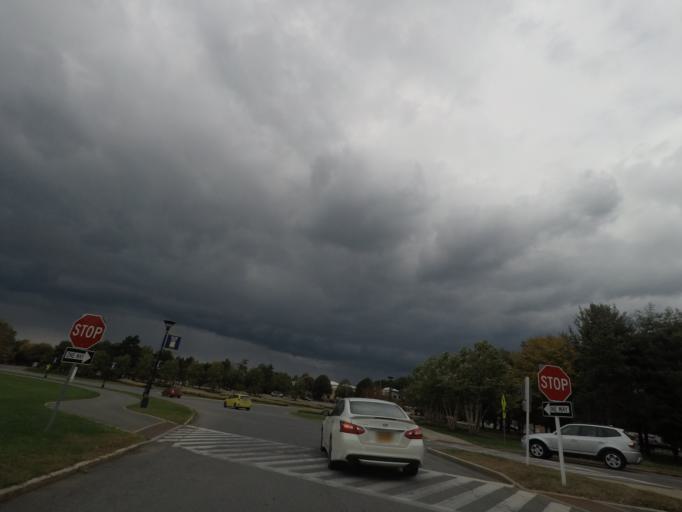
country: US
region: New York
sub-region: Albany County
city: Roessleville
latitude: 42.6884
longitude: -73.8205
